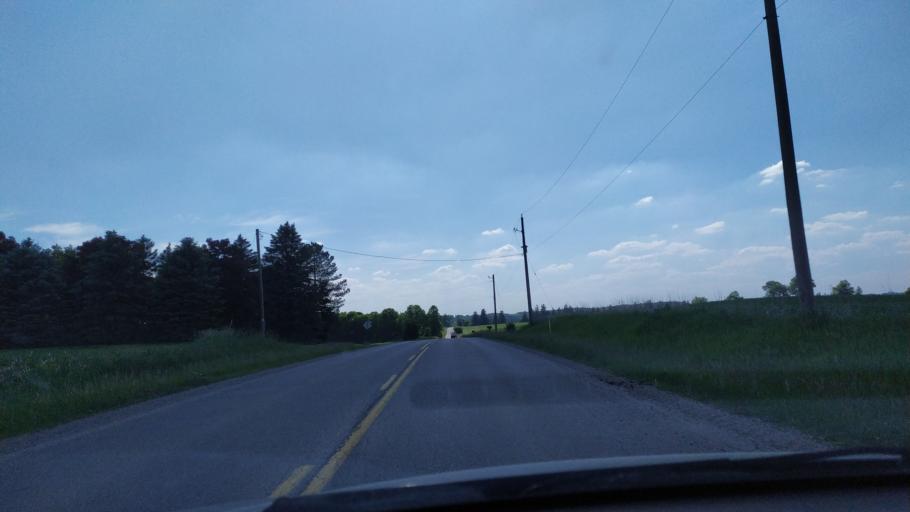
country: CA
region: Ontario
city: Kitchener
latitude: 43.3755
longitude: -80.5298
